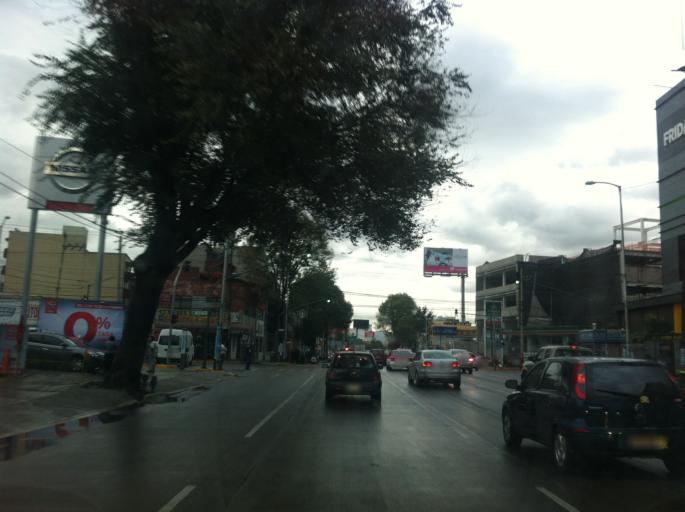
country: MX
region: Mexico City
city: Colonia del Valle
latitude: 19.3966
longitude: -99.1811
